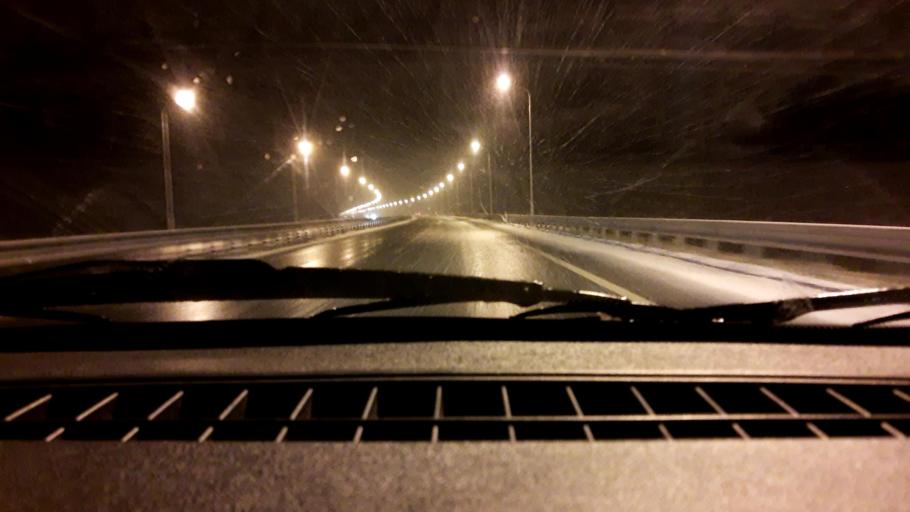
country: RU
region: Bashkortostan
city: Ufa
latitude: 54.6750
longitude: 56.0219
